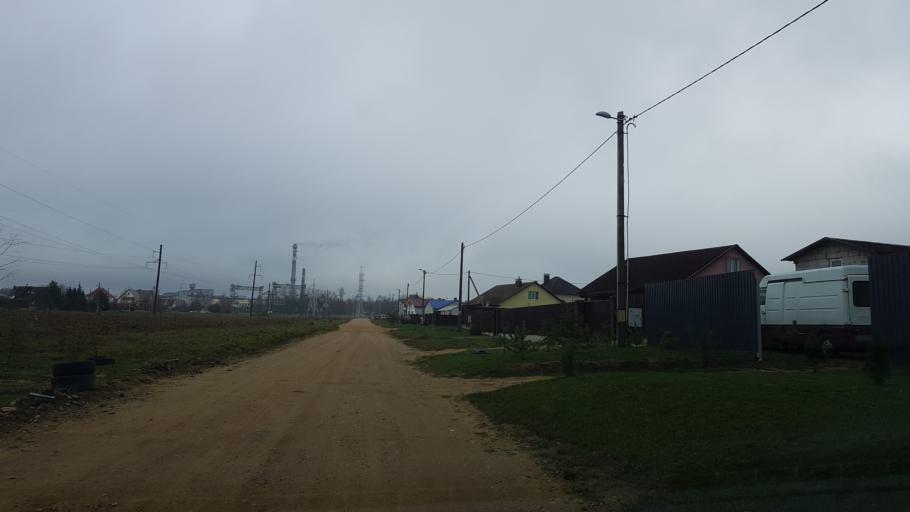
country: BY
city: Fanipol
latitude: 53.7313
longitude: 27.3196
